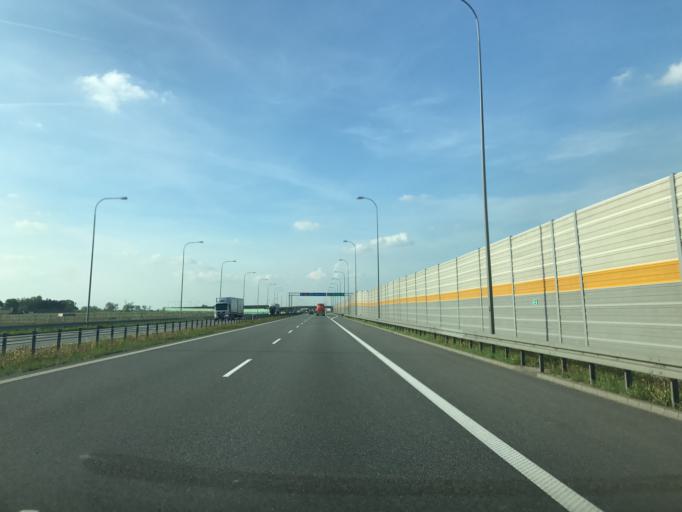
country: PL
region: Kujawsko-Pomorskie
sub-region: Powiat torunski
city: Lubicz Dolny
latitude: 53.0836
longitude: 18.7514
